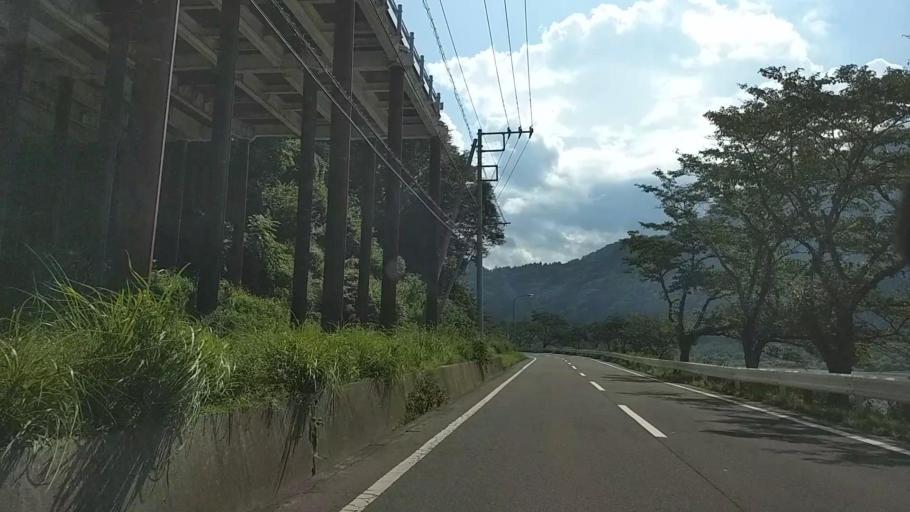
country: JP
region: Shizuoka
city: Fujinomiya
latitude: 35.3987
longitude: 138.4506
